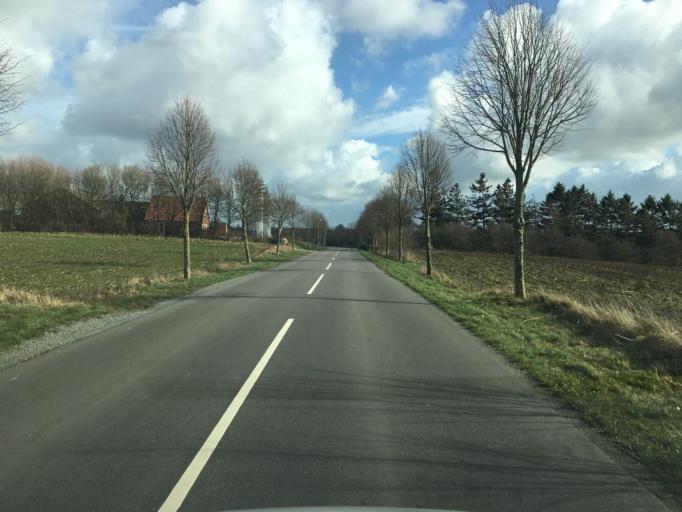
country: DK
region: South Denmark
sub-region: Aabenraa Kommune
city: Krusa
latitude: 54.8977
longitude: 9.4346
